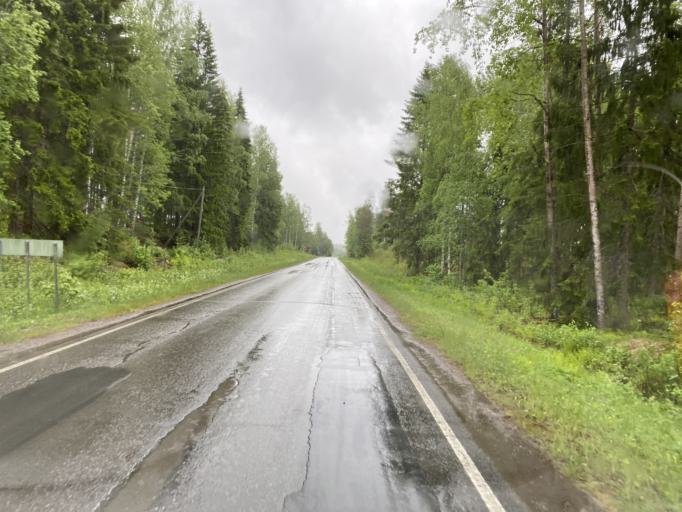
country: FI
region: Pirkanmaa
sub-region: Etelae-Pirkanmaa
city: Urjala
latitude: 61.0393
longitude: 23.4514
